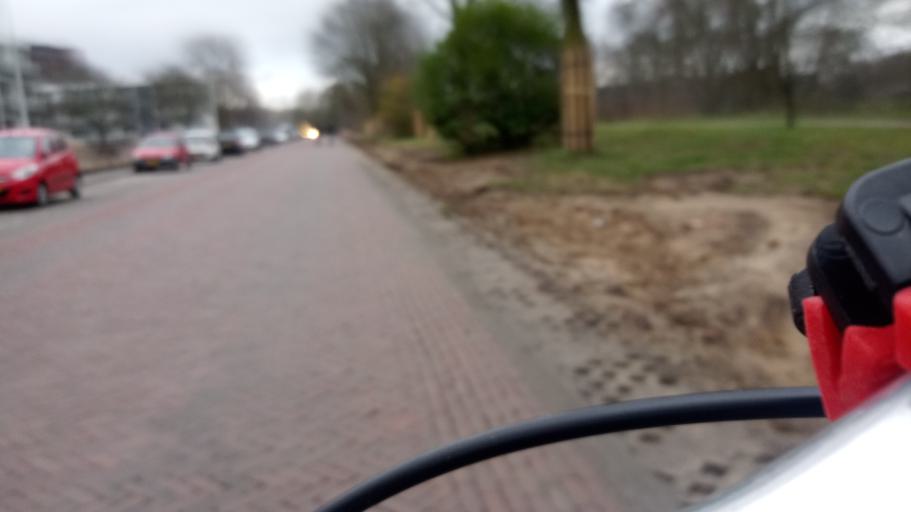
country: NL
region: Gelderland
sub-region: Gemeente Nijmegen
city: Nijmegen
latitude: 51.8056
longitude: 5.8350
